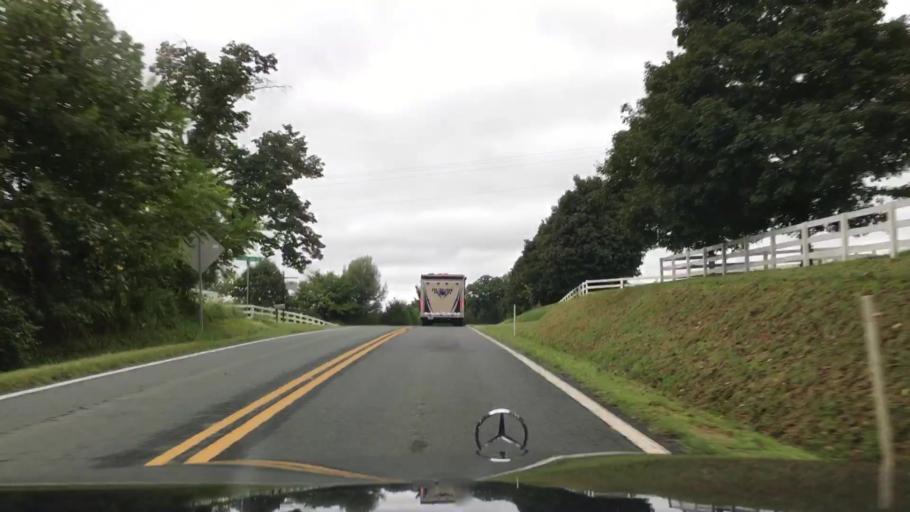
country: US
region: Virginia
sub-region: Orange County
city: Gordonsville
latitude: 38.0808
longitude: -78.2886
